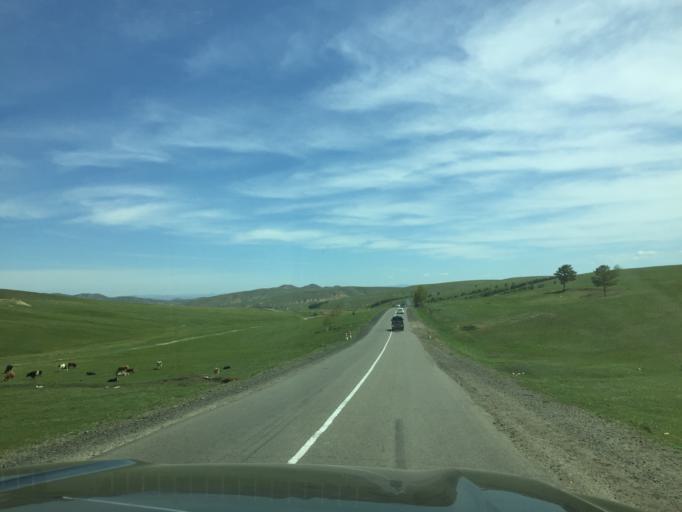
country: MN
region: Central Aimak
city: Javhlant
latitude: 48.6511
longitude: 106.1031
